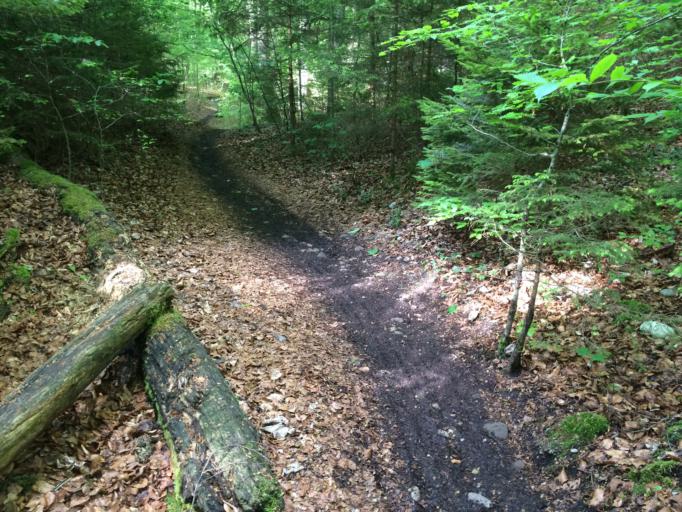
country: DE
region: Bavaria
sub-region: Upper Bavaria
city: Pullach im Isartal
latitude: 48.0542
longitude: 11.5266
